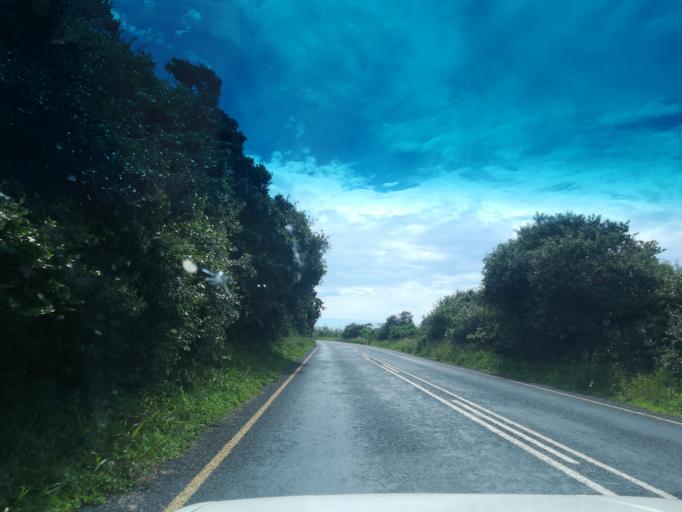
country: ZA
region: KwaZulu-Natal
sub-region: Ugu District Municipality
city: Scottburgh
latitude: -30.3430
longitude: 30.7295
